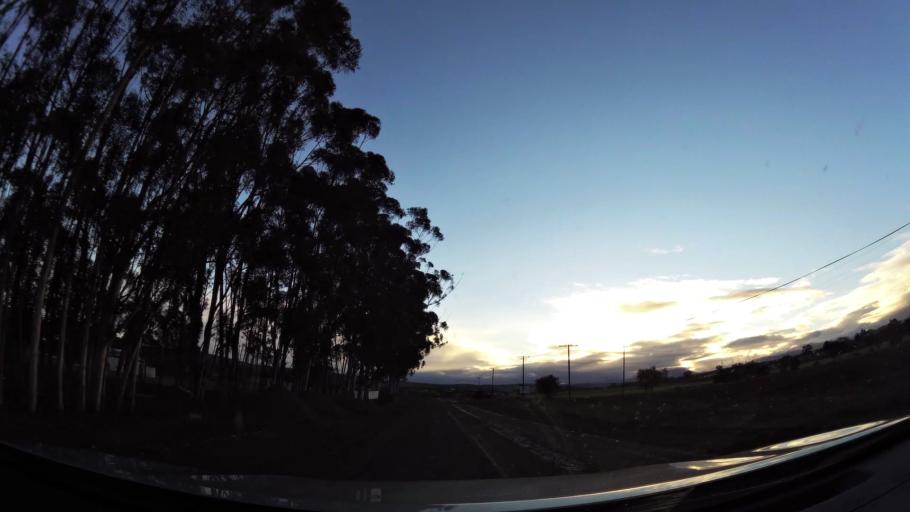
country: ZA
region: Western Cape
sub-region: Eden District Municipality
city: Riversdale
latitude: -34.0815
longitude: 20.9391
